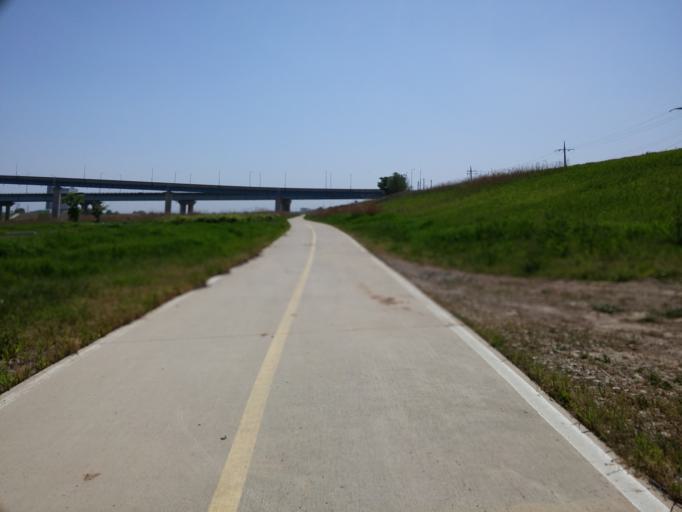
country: KR
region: Chungcheongnam-do
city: Nonsan
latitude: 36.2096
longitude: 127.0775
